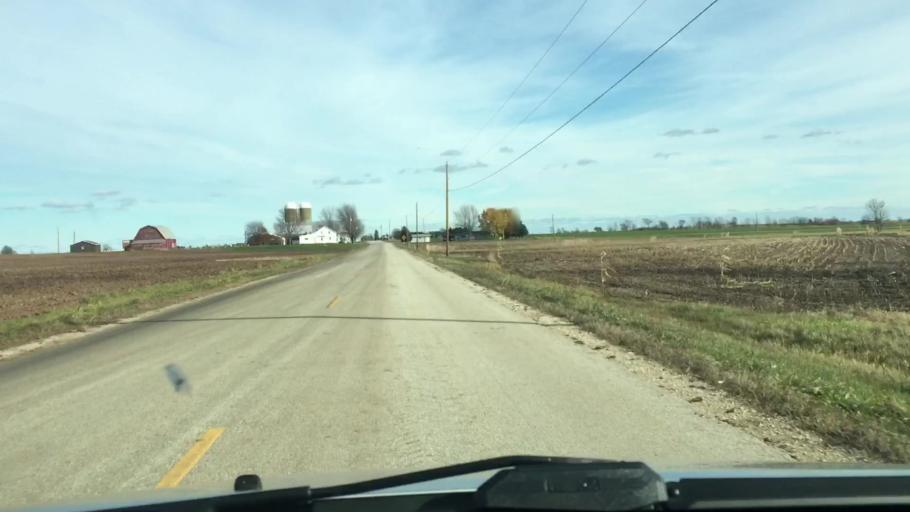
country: US
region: Wisconsin
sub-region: Kewaunee County
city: Luxemburg
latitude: 44.6973
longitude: -87.6048
